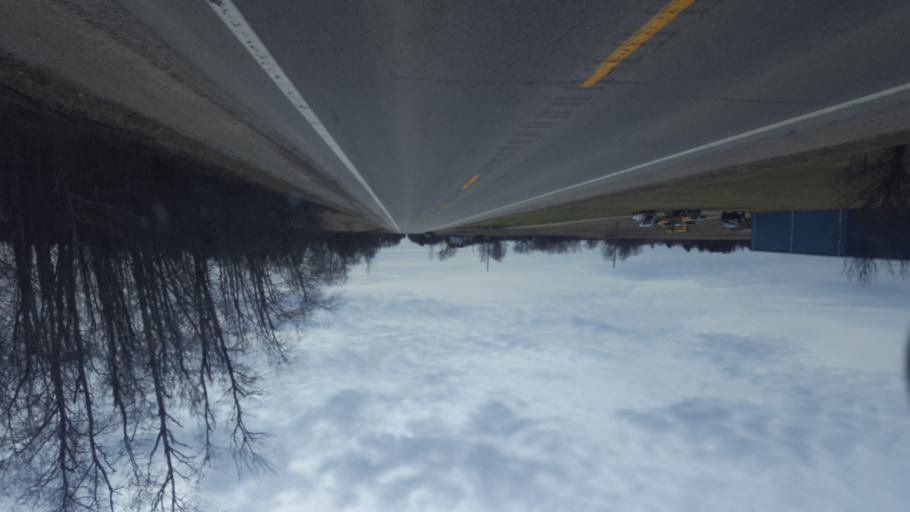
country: US
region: Michigan
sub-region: Isabella County
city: Lake Isabella
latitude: 43.7039
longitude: -85.1467
